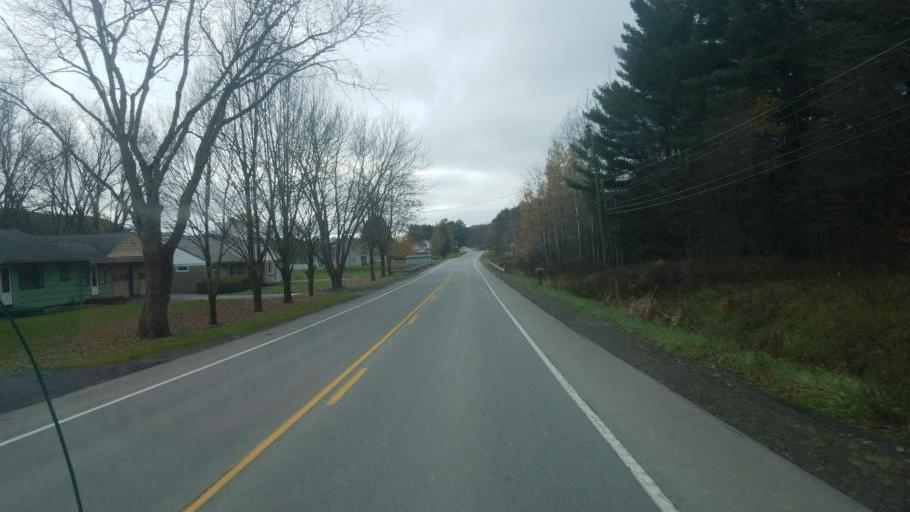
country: US
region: Pennsylvania
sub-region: Jefferson County
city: Brockway
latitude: 41.2719
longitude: -78.7112
